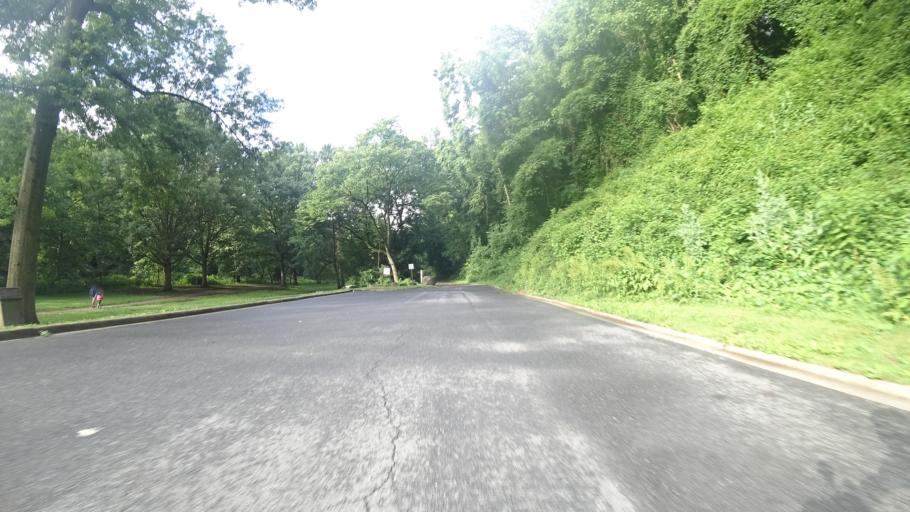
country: US
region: Maryland
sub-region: Montgomery County
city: Chevy Chase
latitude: 38.9438
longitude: -77.0506
